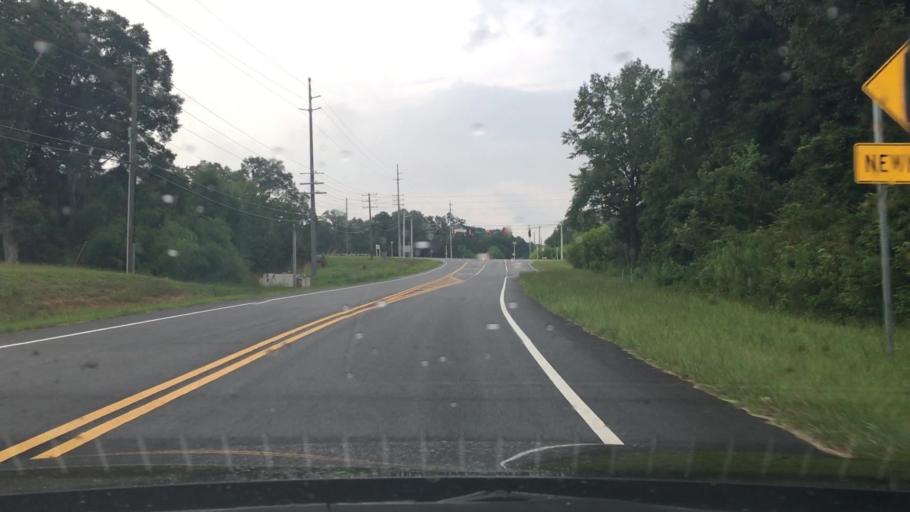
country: US
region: Georgia
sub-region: Spalding County
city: Experiment
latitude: 33.2425
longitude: -84.3832
